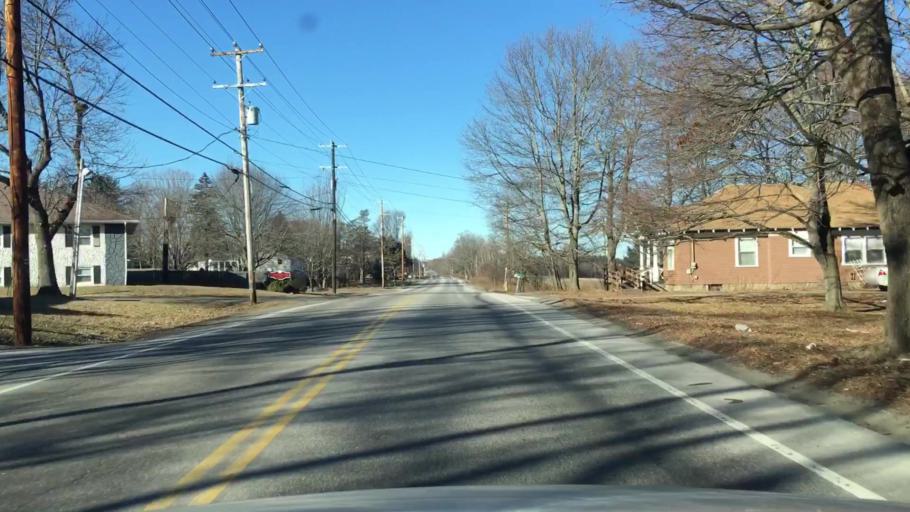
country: US
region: Maine
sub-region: Penobscot County
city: Bangor
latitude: 44.8188
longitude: -68.8021
